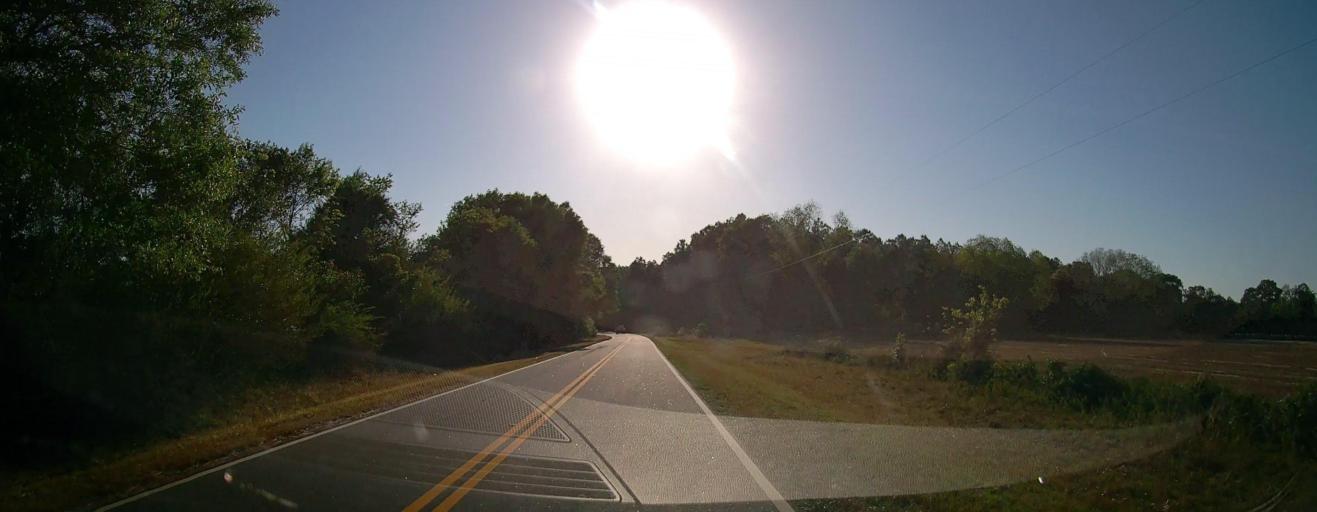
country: US
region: Georgia
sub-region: Ben Hill County
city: Fitzgerald
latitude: 31.6587
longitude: -83.1550
